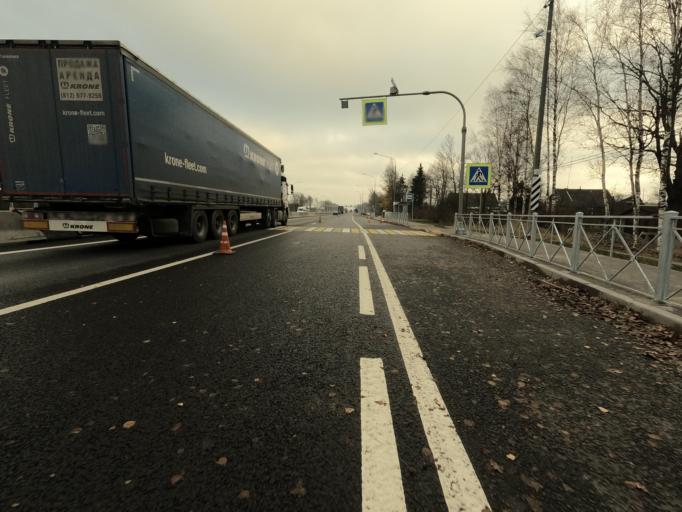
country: RU
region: Leningrad
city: Mga
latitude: 59.7247
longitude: 31.0951
